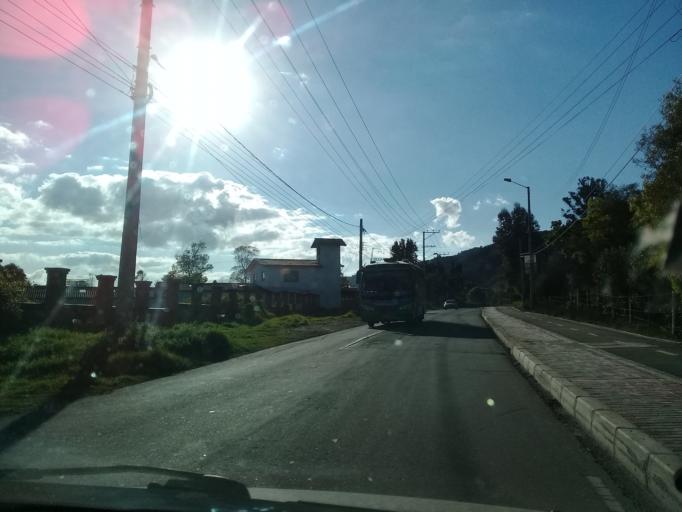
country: CO
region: Cundinamarca
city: Tenjo
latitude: 4.8817
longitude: -74.1254
